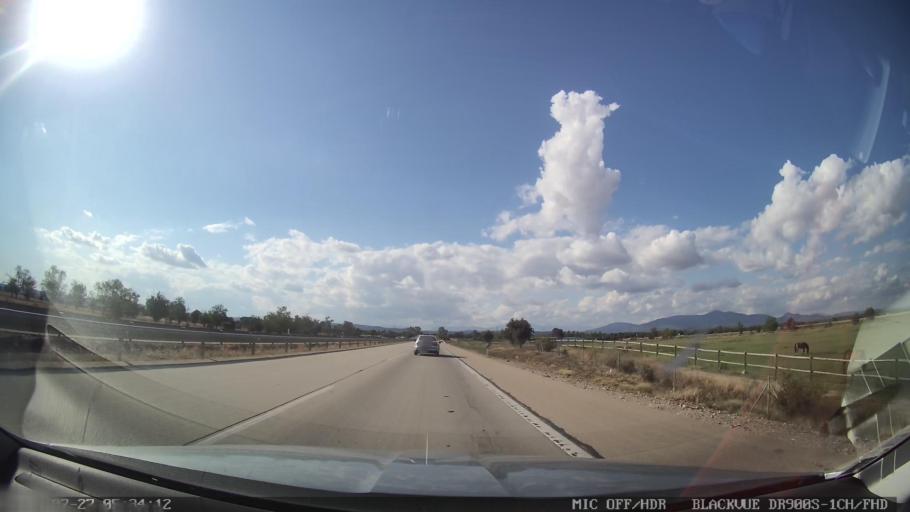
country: ES
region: Castille-La Mancha
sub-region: Province of Toledo
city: Talavera de la Reina
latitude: 39.9898
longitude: -4.7578
